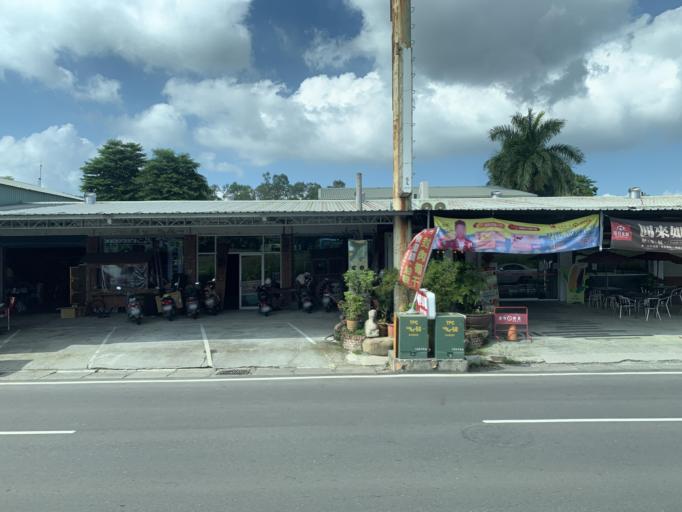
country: TW
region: Taiwan
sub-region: Pingtung
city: Pingtung
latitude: 22.8778
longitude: 120.4969
